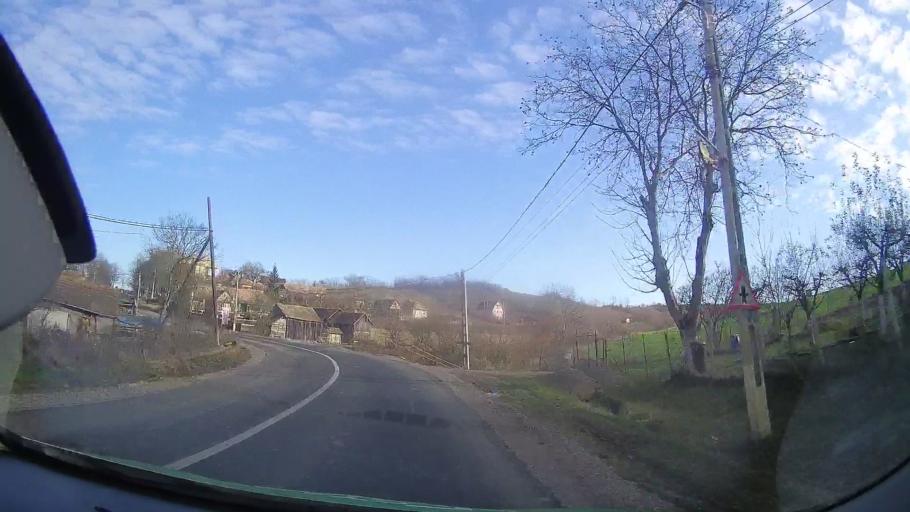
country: RO
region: Mures
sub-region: Comuna Iclanzel
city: Iclanzel
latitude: 46.5229
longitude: 24.2746
